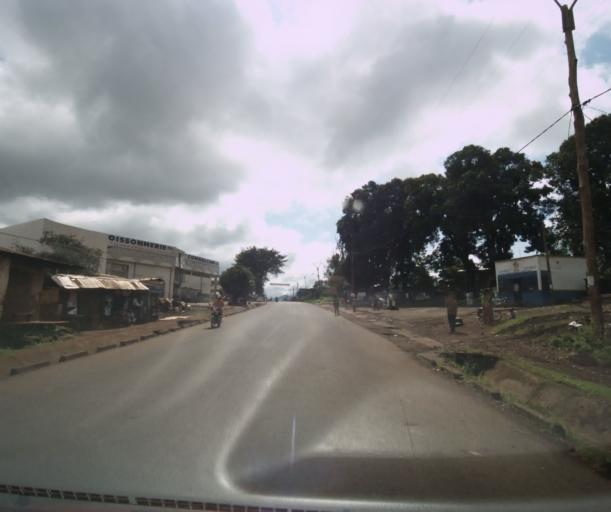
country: CM
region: West
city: Foumbot
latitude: 5.5082
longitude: 10.6319
